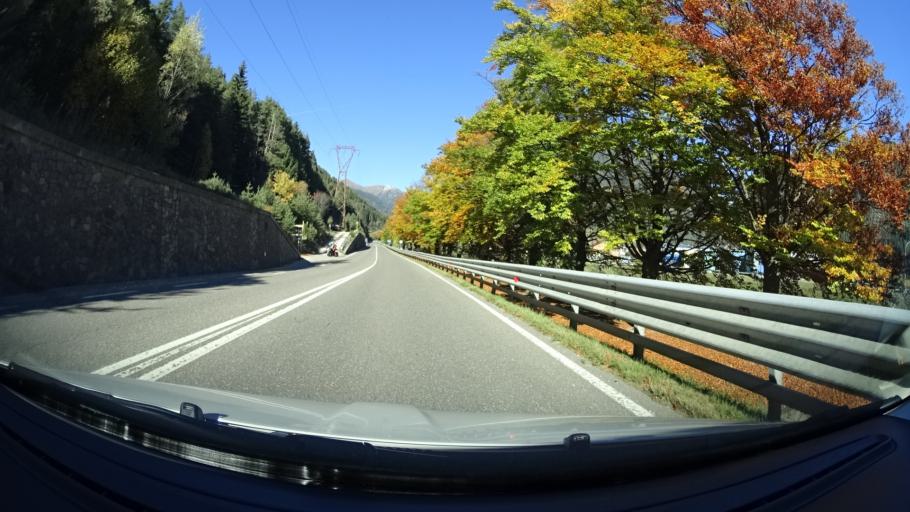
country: IT
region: Trentino-Alto Adige
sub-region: Provincia di Trento
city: Predazzo
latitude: 46.3025
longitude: 11.5907
